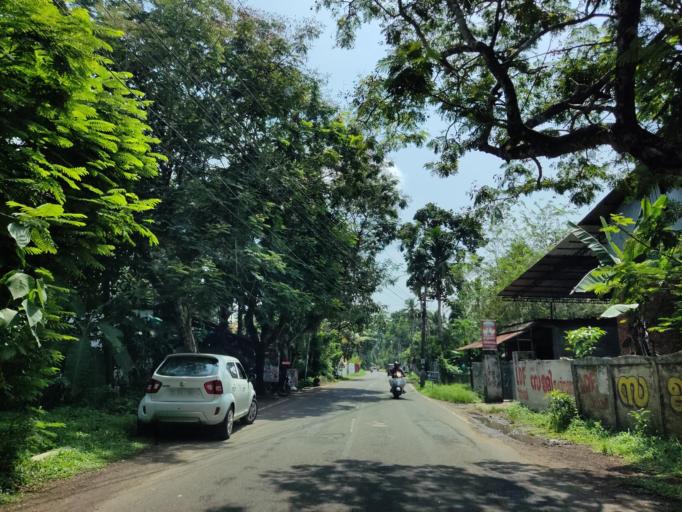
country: IN
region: Kerala
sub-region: Alappuzha
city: Chengannur
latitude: 9.3082
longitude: 76.5710
